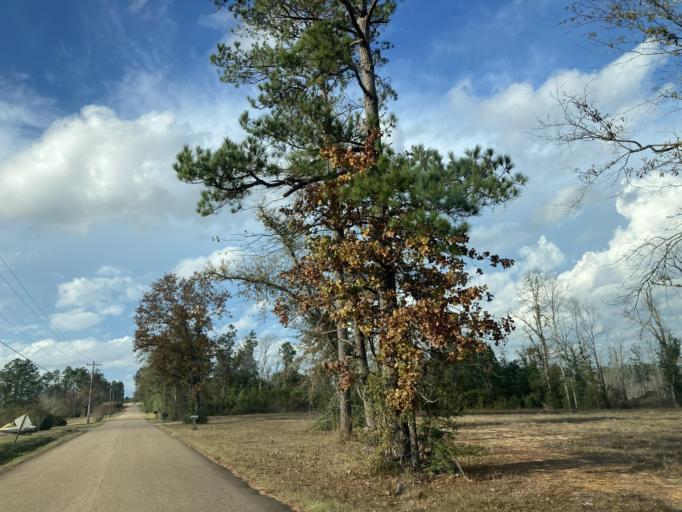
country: US
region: Mississippi
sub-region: Lamar County
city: Purvis
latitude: 31.1333
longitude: -89.6171
